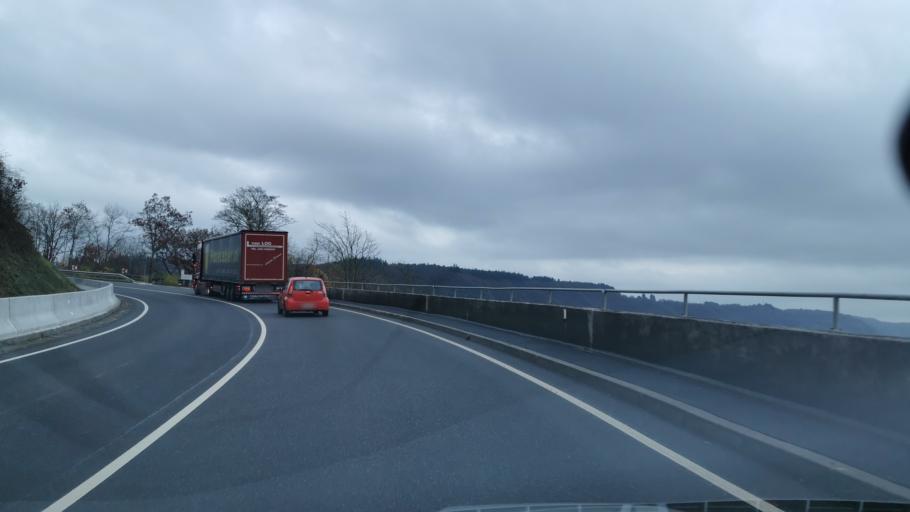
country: DE
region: Rheinland-Pfalz
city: Cochem
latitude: 50.1345
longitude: 7.1730
